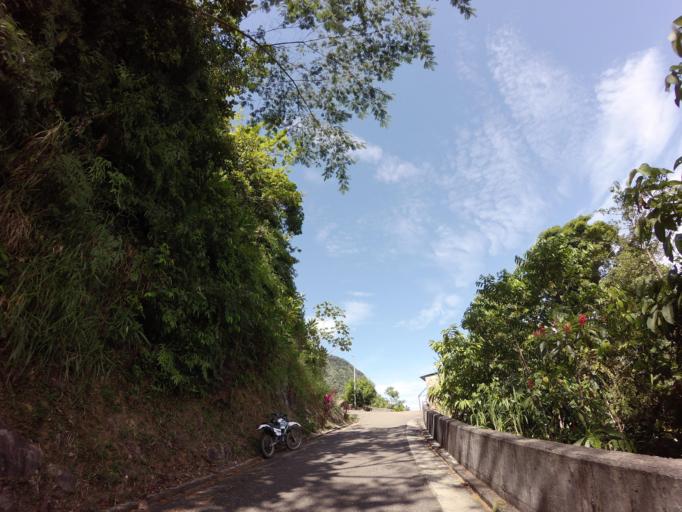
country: CO
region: Caldas
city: Norcasia
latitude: 5.5664
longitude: -74.9058
